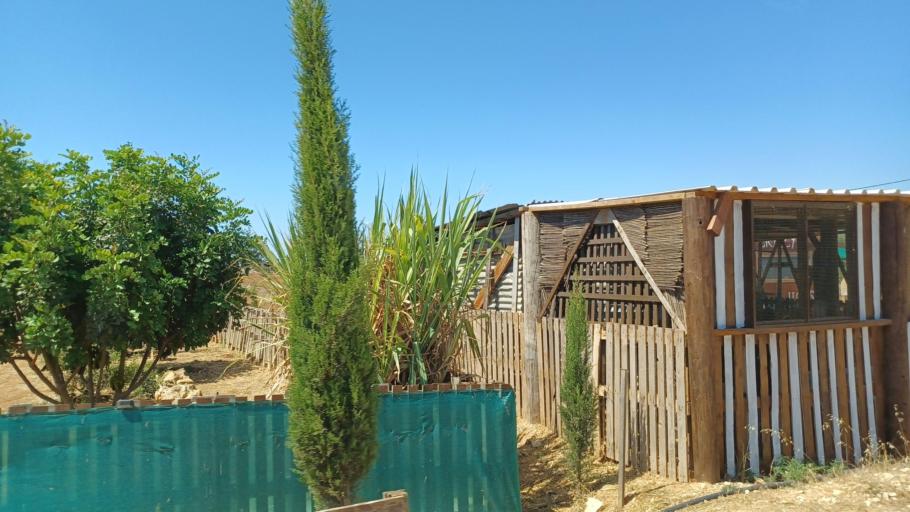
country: CY
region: Larnaka
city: Xylotymbou
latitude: 35.0290
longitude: 33.7313
